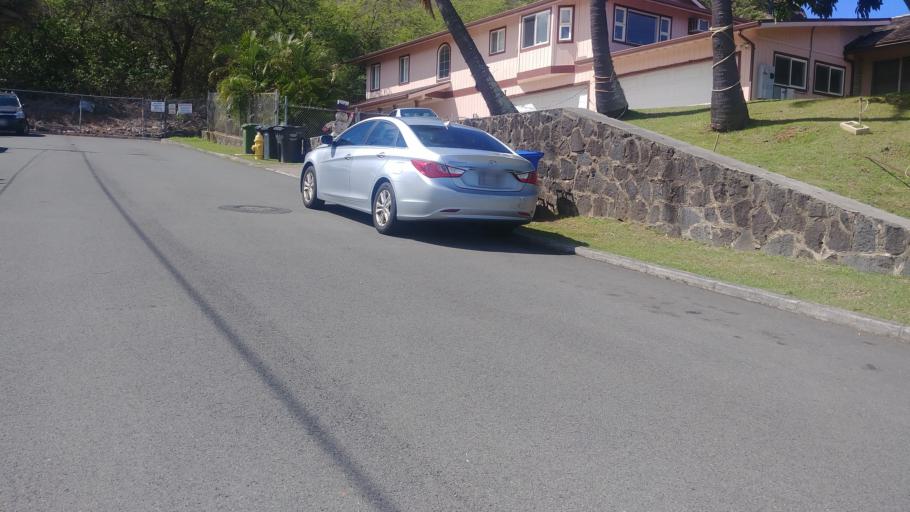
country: US
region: Hawaii
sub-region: Honolulu County
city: Honolulu
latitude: 21.2684
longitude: -157.8103
